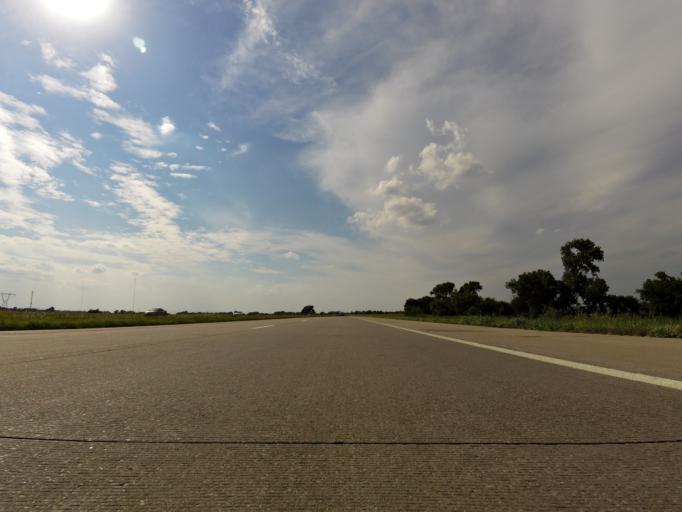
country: US
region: Kansas
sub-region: Sedgwick County
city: Maize
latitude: 37.7973
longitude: -97.4844
